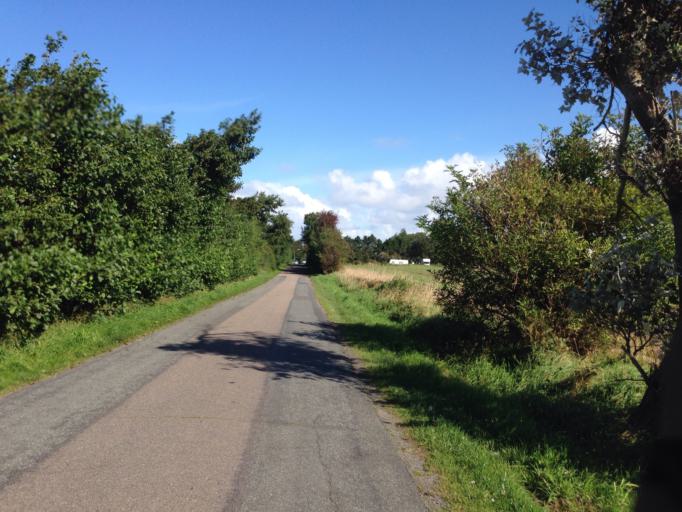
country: DE
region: Schleswig-Holstein
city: Borgsum
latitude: 54.6969
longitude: 8.4535
